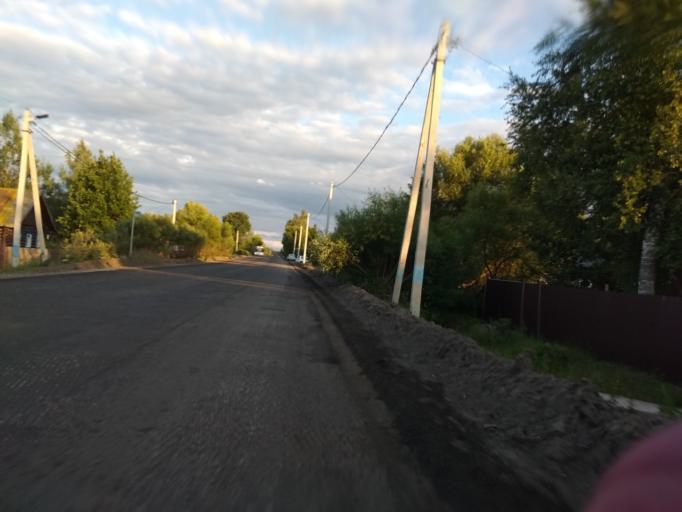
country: RU
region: Moskovskaya
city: Misheronskiy
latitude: 55.6535
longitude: 39.7531
